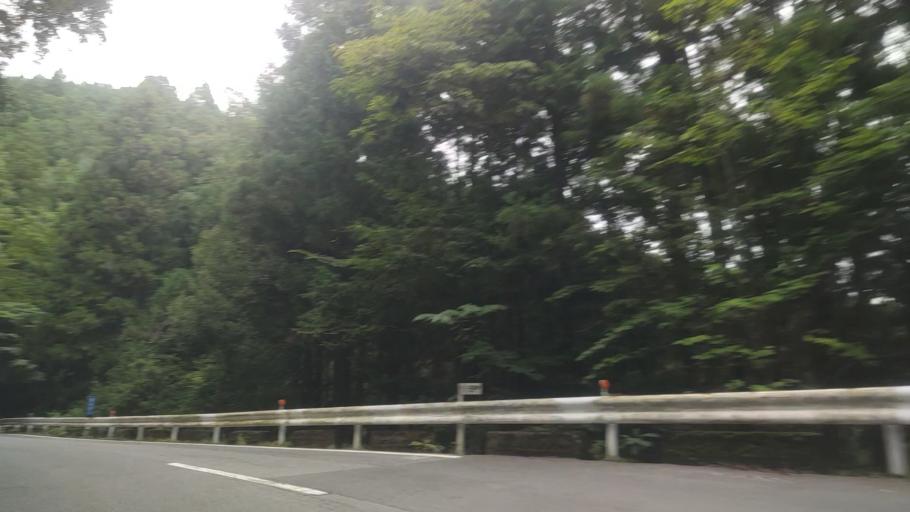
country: JP
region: Wakayama
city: Koya
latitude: 34.2099
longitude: 135.5446
